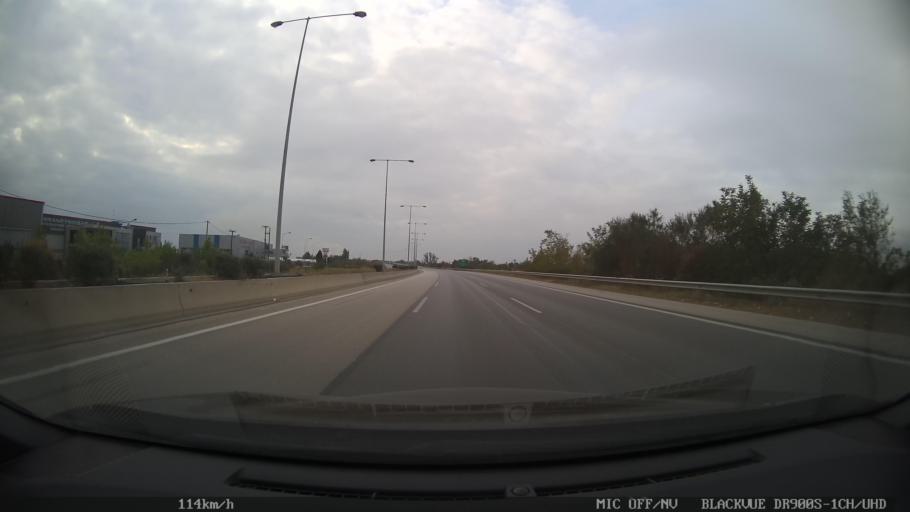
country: GR
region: Central Macedonia
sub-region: Nomos Thessalonikis
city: Nea Magnisia
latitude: 40.6765
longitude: 22.8322
